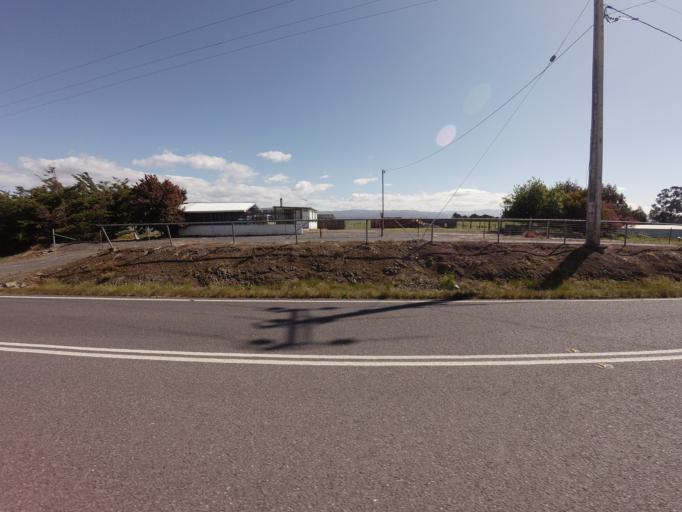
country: AU
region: Tasmania
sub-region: Derwent Valley
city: New Norfolk
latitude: -42.6986
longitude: 146.9433
